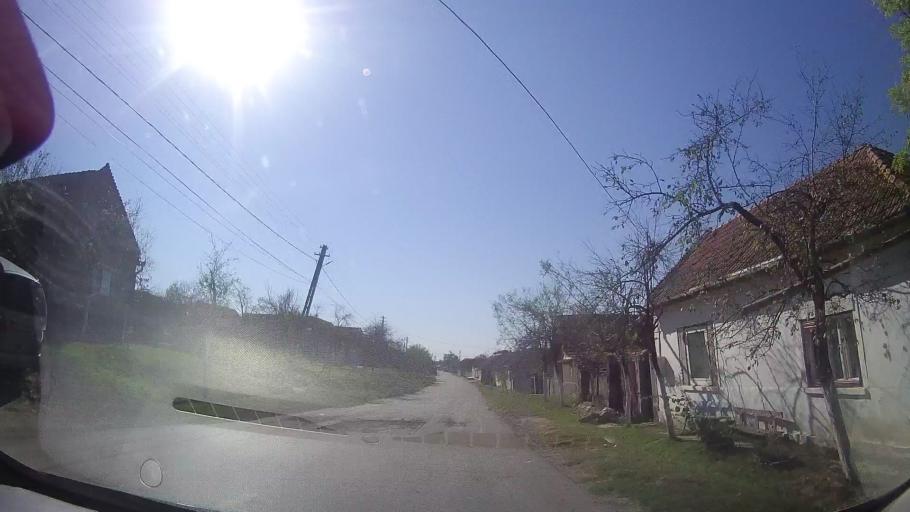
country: RO
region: Timis
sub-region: Comuna Bethausen
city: Bethausen
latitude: 45.8602
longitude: 21.9692
